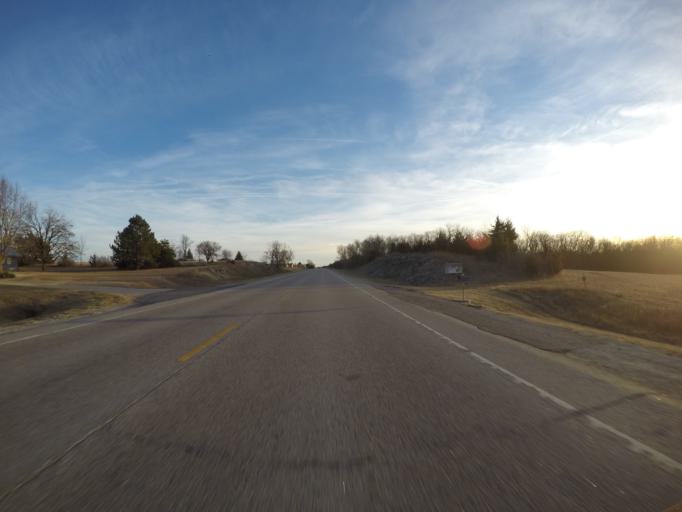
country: US
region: Kansas
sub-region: Marshall County
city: Blue Rapids
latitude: 39.4191
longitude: -96.7645
